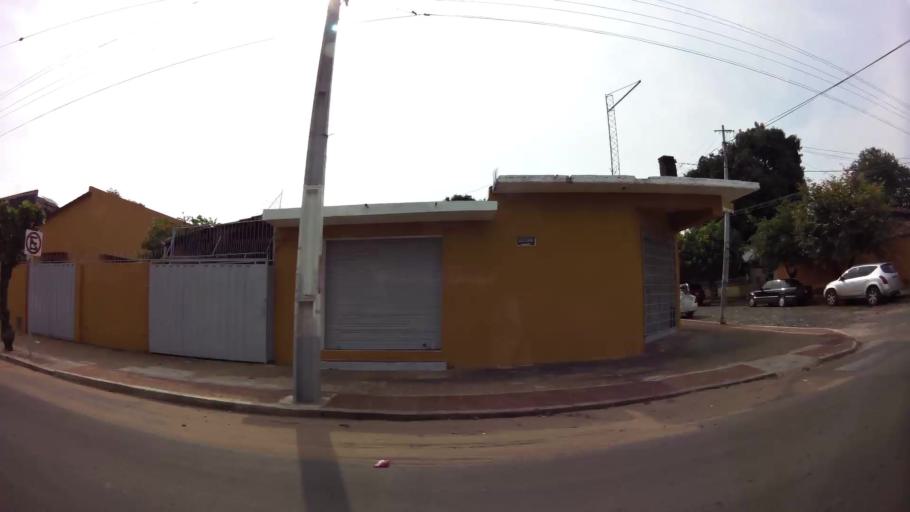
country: PY
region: Central
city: Fernando de la Mora
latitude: -25.2992
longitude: -57.5560
